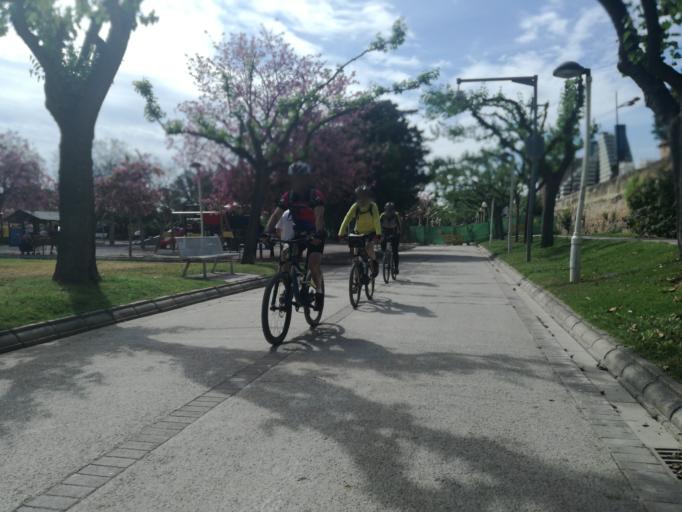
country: ES
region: Valencia
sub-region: Provincia de Valencia
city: Valencia
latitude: 39.4609
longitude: -0.3594
